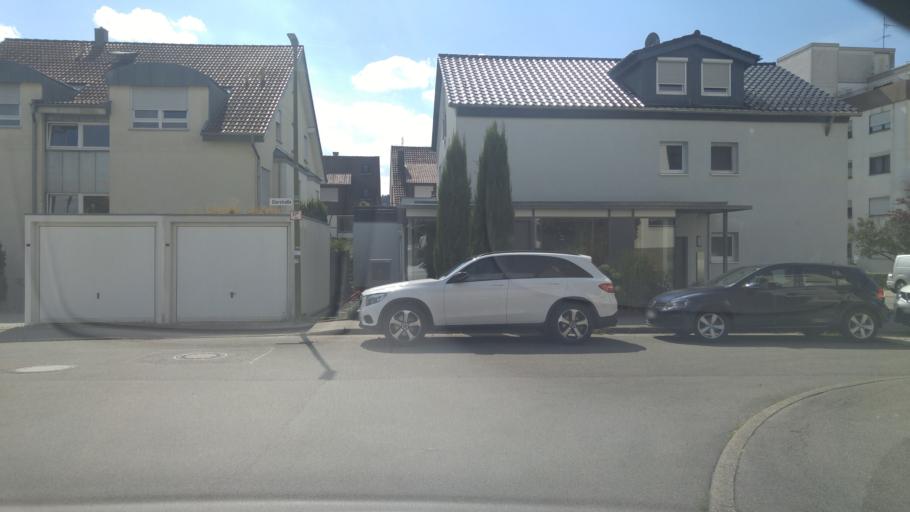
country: DE
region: Baden-Wuerttemberg
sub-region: Regierungsbezirk Stuttgart
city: Leonberg
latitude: 48.7892
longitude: 9.0117
